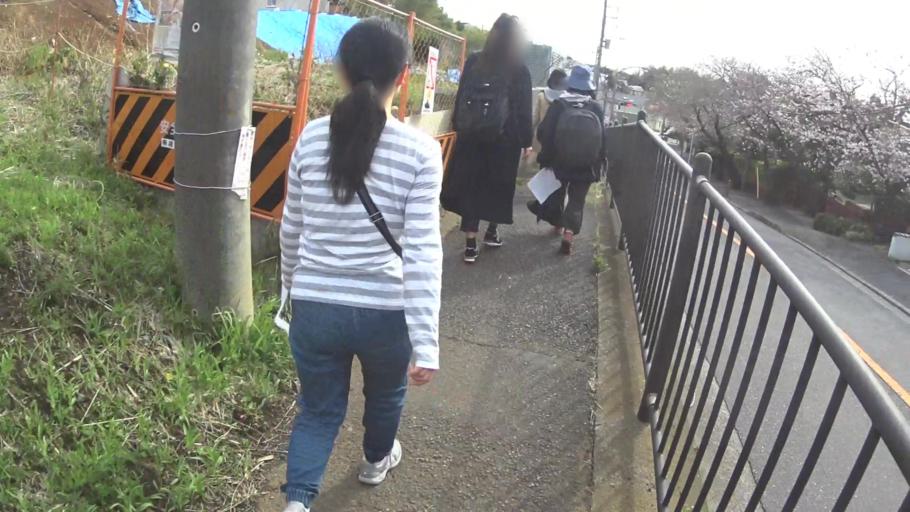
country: JP
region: Kanagawa
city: Kamakura
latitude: 35.3235
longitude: 139.5135
